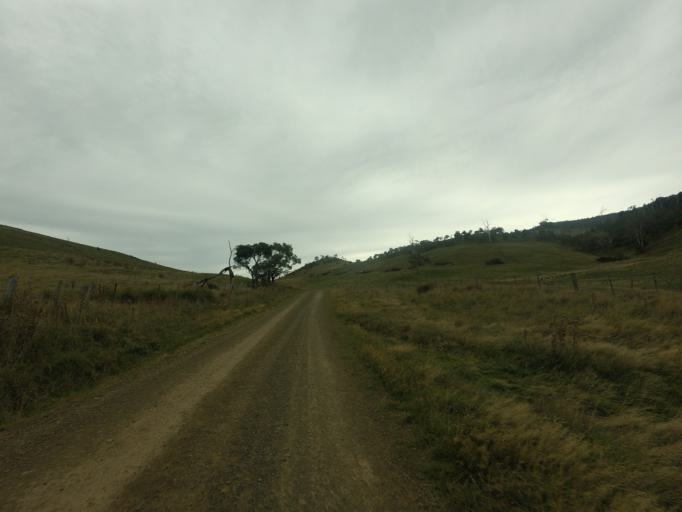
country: AU
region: Tasmania
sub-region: Derwent Valley
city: New Norfolk
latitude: -42.3764
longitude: 146.8642
